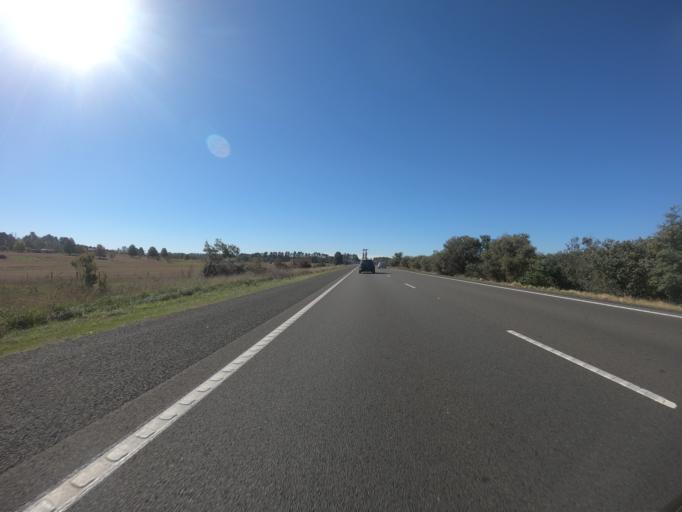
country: AU
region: New South Wales
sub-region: Wingecarribee
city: Moss Vale
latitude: -34.5402
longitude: 150.2775
